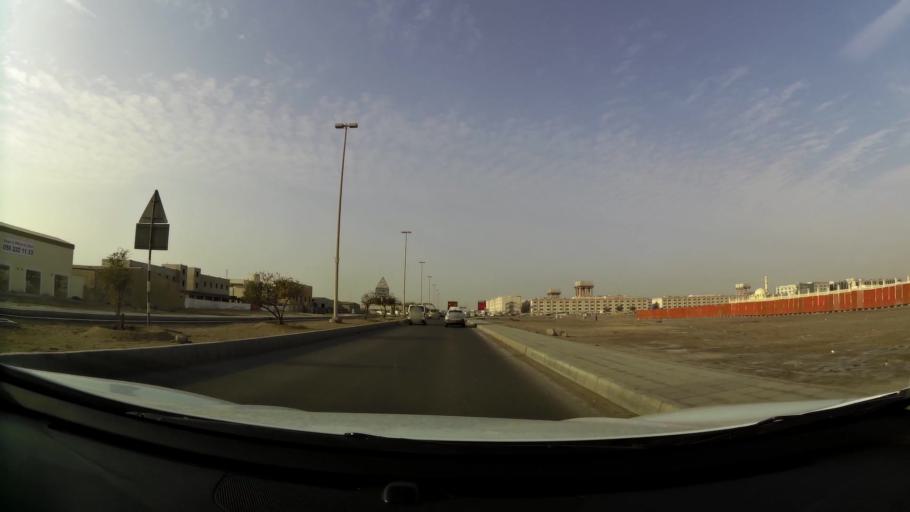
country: AE
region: Abu Dhabi
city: Abu Dhabi
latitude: 24.3569
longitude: 54.5168
